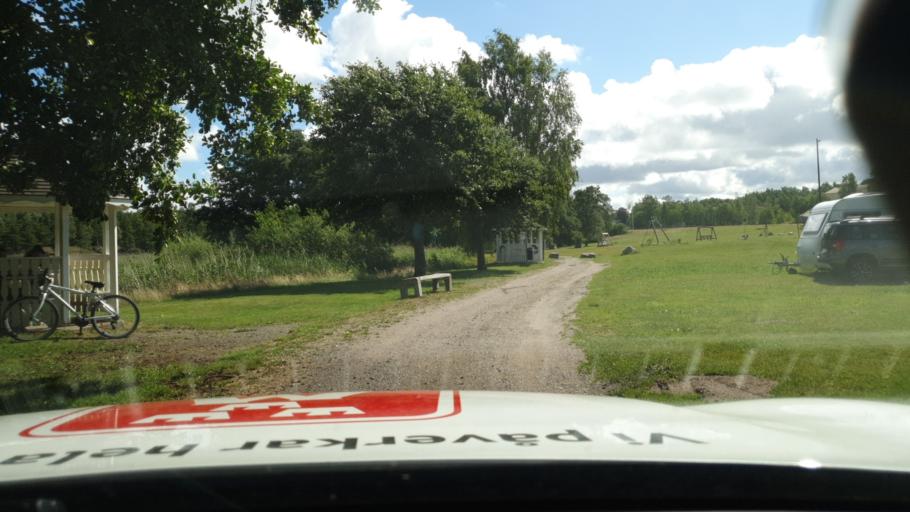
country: SE
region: Vaestra Goetaland
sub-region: Gullspangs Kommun
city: Gullspang
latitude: 58.9884
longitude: 14.0966
